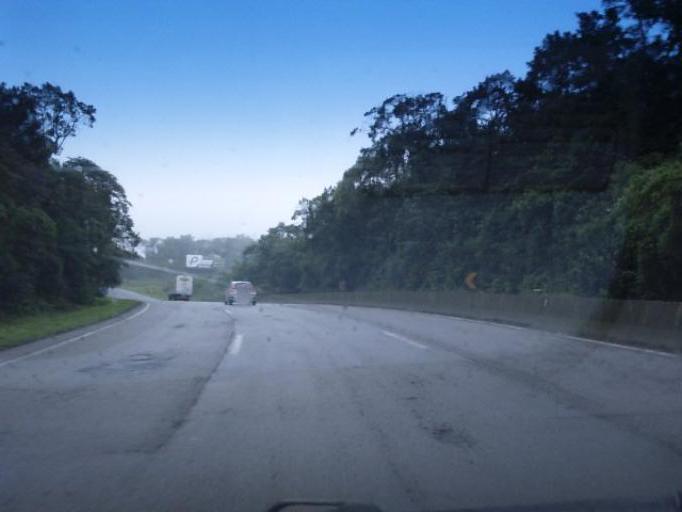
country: BR
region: Parana
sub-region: Antonina
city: Antonina
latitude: -25.1105
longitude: -48.7854
